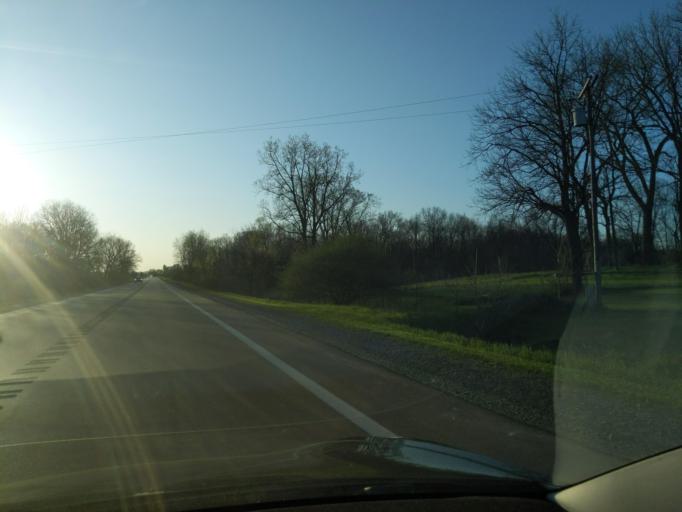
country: US
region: Michigan
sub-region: Ingham County
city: Stockbridge
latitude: 42.4078
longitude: -84.1246
